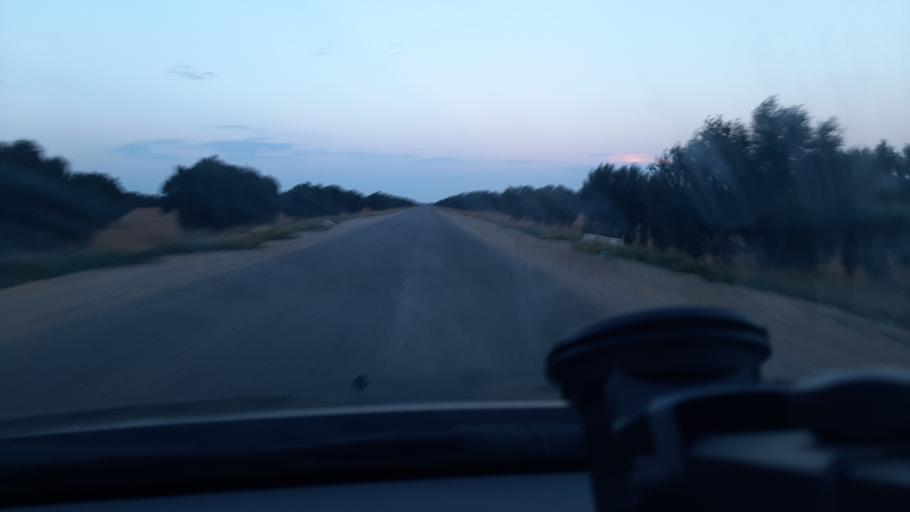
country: TN
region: Al Mahdiyah
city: Shurban
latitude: 34.9952
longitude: 10.4038
